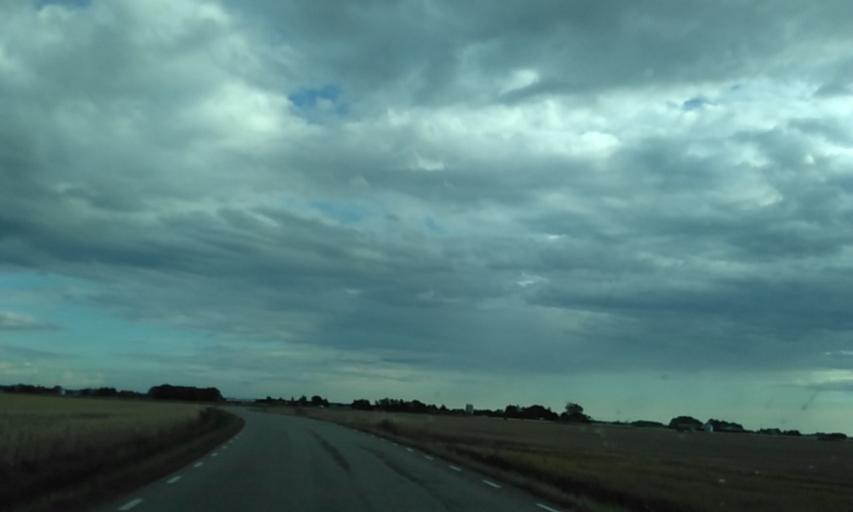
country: SE
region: Vaestra Goetaland
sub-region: Grastorps Kommun
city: Graestorp
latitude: 58.4215
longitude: 12.7261
